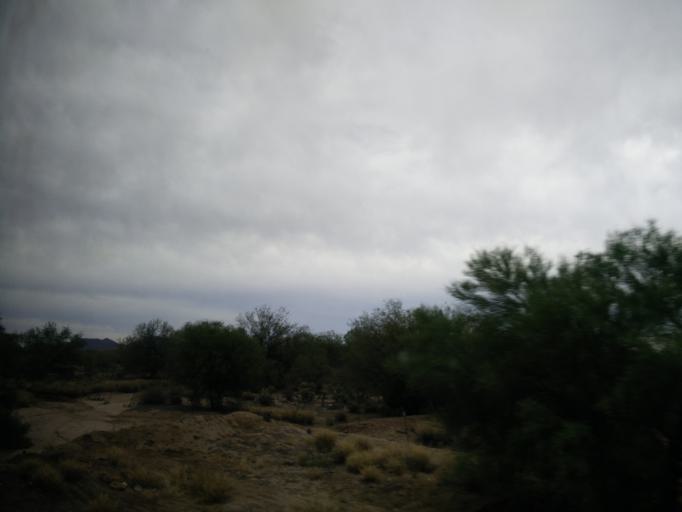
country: MX
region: Sonora
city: Hermosillo
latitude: 28.7256
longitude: -110.9798
